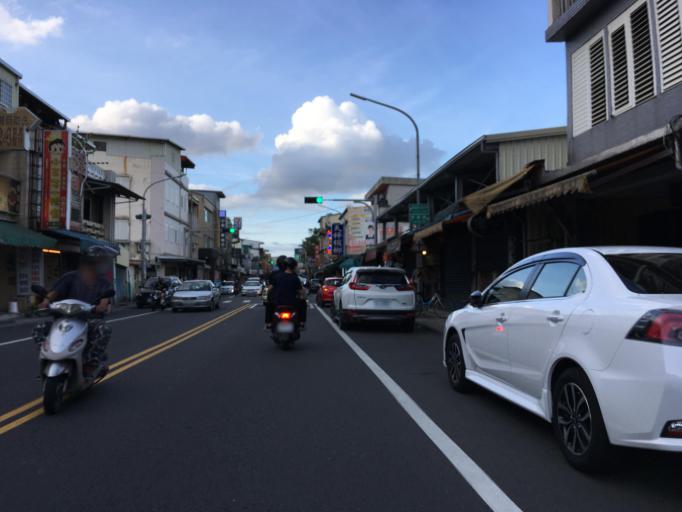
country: TW
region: Taiwan
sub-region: Yilan
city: Yilan
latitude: 24.6655
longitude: 121.7675
